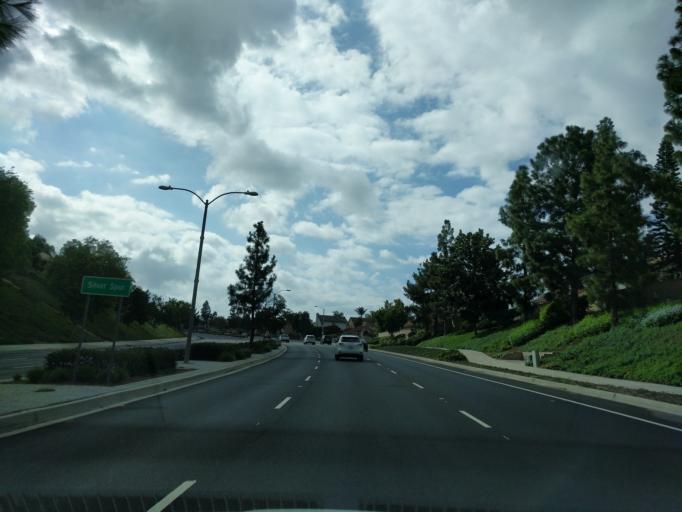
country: US
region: California
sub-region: Orange County
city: Aliso Viejo
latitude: 33.5604
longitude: -117.7034
